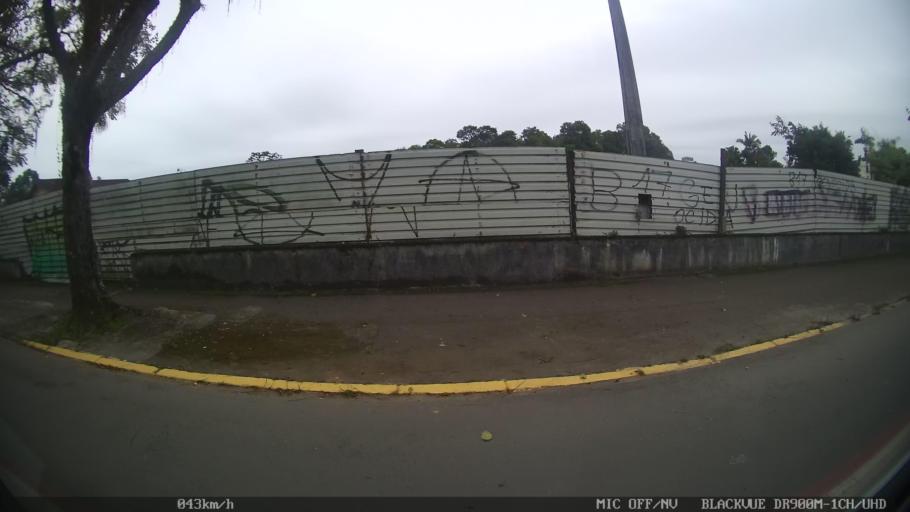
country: BR
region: Santa Catarina
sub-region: Joinville
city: Joinville
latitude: -26.2899
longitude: -48.8405
